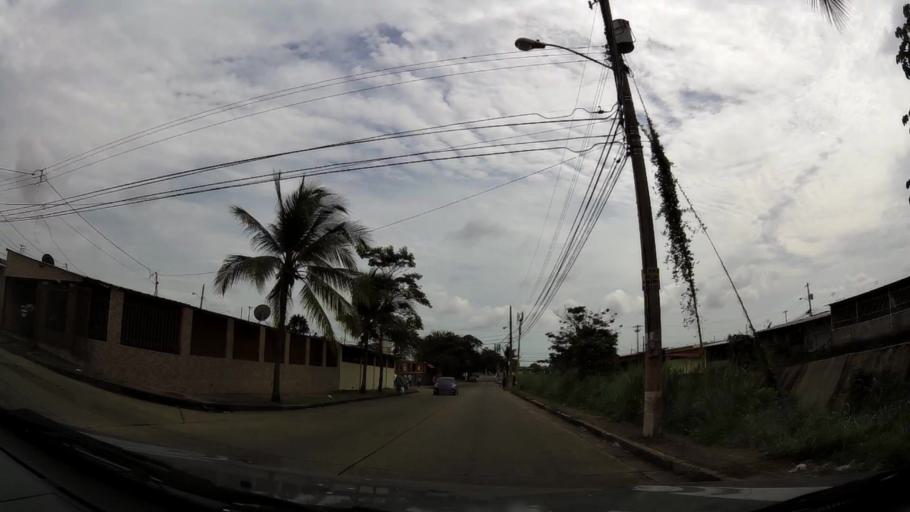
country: PA
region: Panama
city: Tocumen
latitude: 9.0550
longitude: -79.4189
